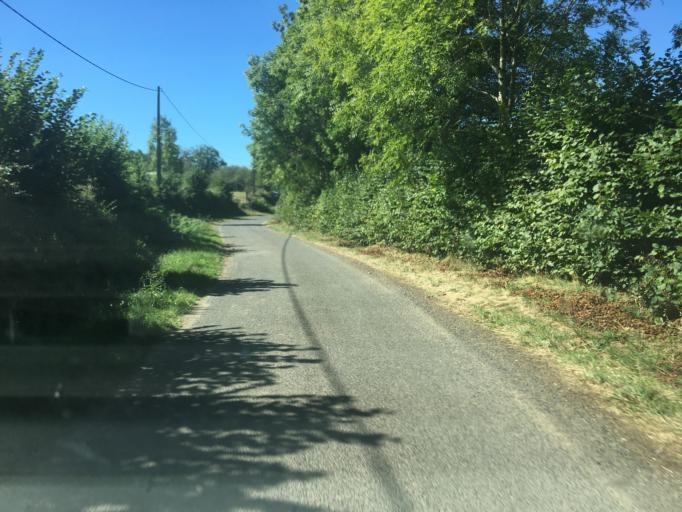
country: FR
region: Limousin
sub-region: Departement de la Correze
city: Bort-les-Orgues
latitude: 45.3994
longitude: 2.4784
